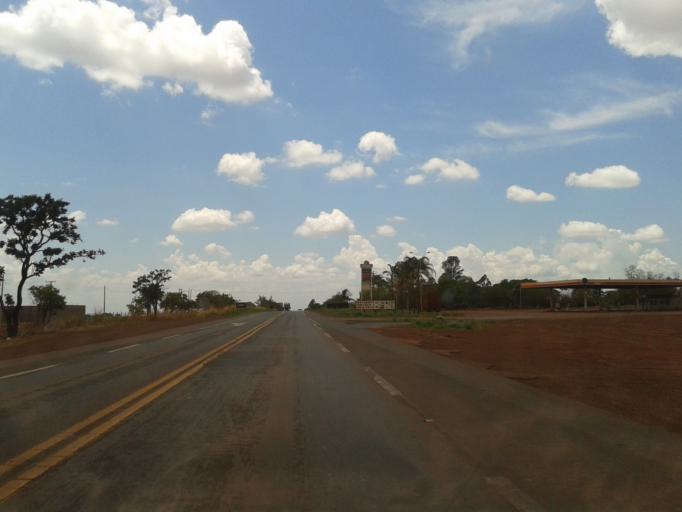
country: BR
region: Goias
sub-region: Goiatuba
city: Goiatuba
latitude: -18.2443
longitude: -49.7016
